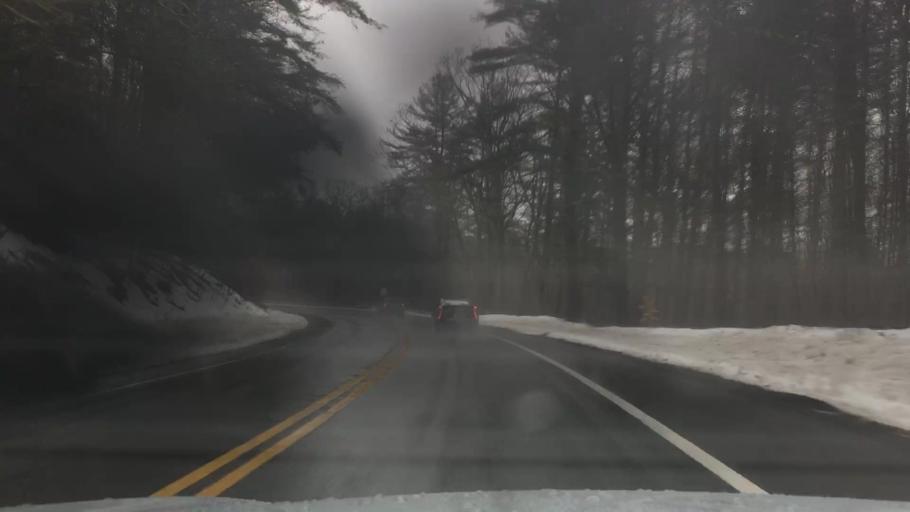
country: US
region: Massachusetts
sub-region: Franklin County
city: Shutesbury
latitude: 42.4358
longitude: -72.3903
